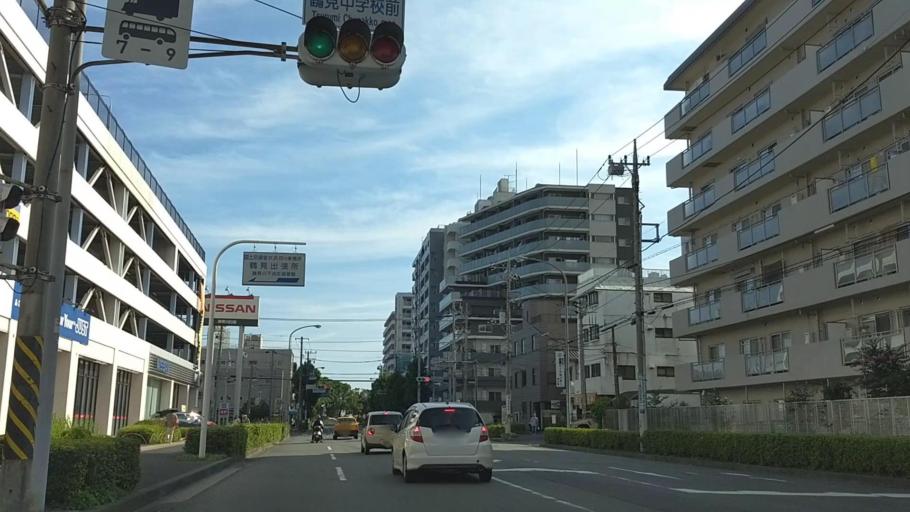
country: JP
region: Kanagawa
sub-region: Kawasaki-shi
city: Kawasaki
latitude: 35.5087
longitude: 139.6852
